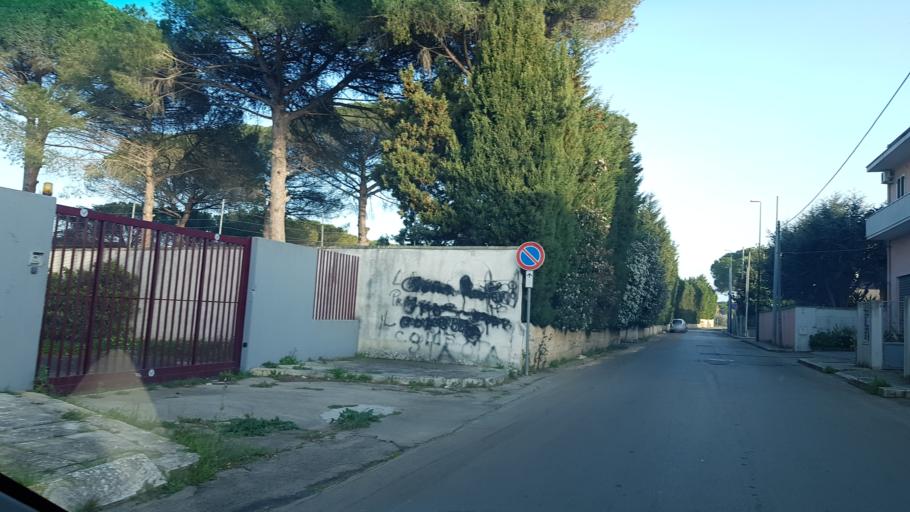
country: IT
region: Apulia
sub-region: Provincia di Lecce
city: Campi Salentina
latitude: 40.3961
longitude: 18.0265
